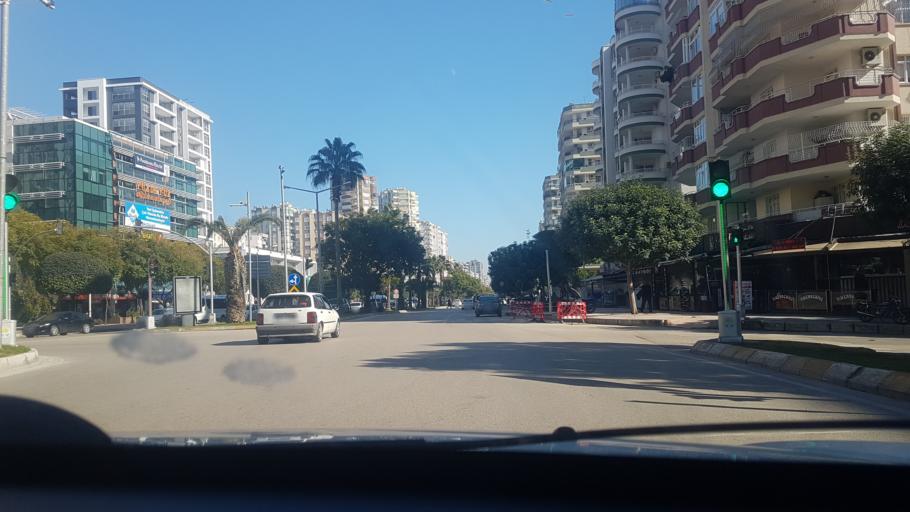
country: TR
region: Adana
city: Adana
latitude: 37.0483
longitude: 35.2864
